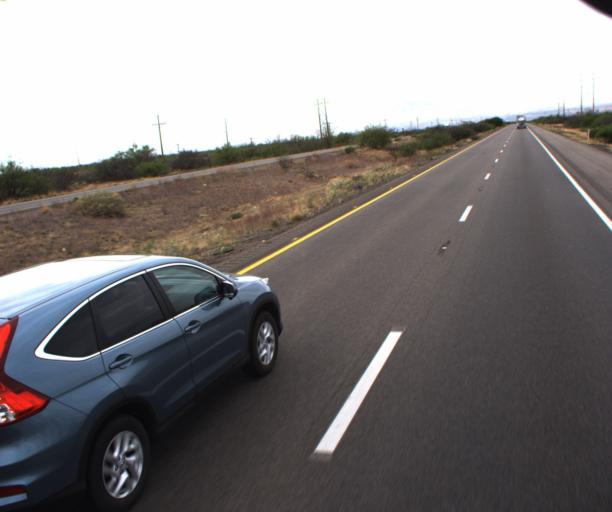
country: US
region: Arizona
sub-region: Cochise County
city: Saint David
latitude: 32.0007
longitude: -110.1547
